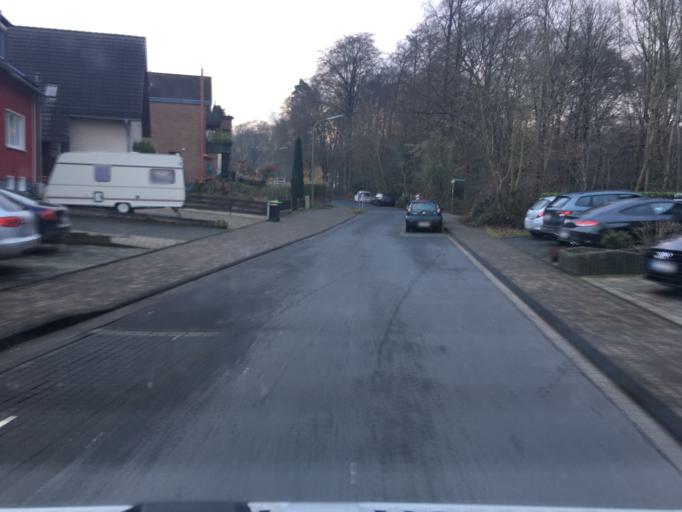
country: DE
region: North Rhine-Westphalia
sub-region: Regierungsbezirk Koln
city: Odenthal
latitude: 51.0150
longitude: 7.1151
